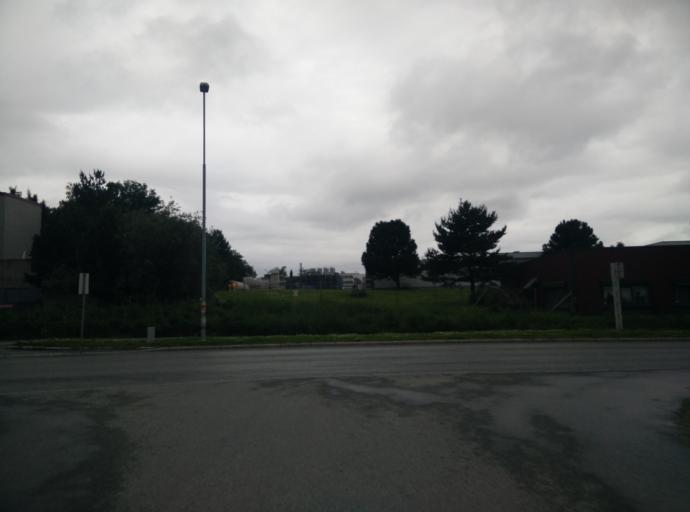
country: NO
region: Sor-Trondelag
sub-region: Trondheim
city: Trondheim
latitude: 63.4271
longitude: 10.4743
